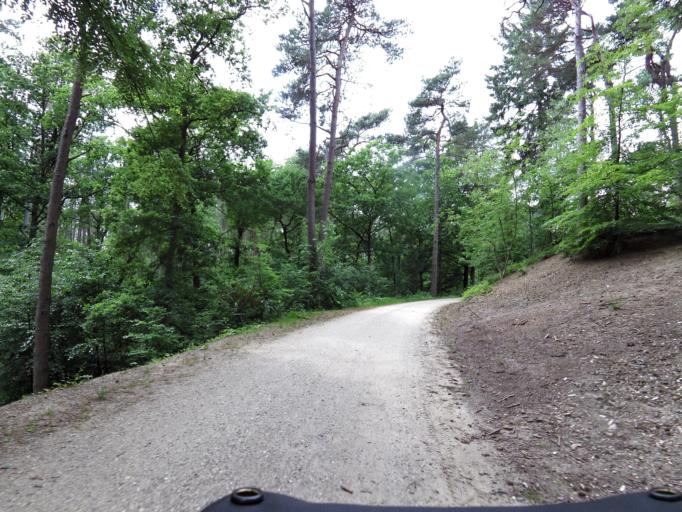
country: NL
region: Gelderland
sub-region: Gemeente Apeldoorn
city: Loenen
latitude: 52.1350
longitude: 6.0132
